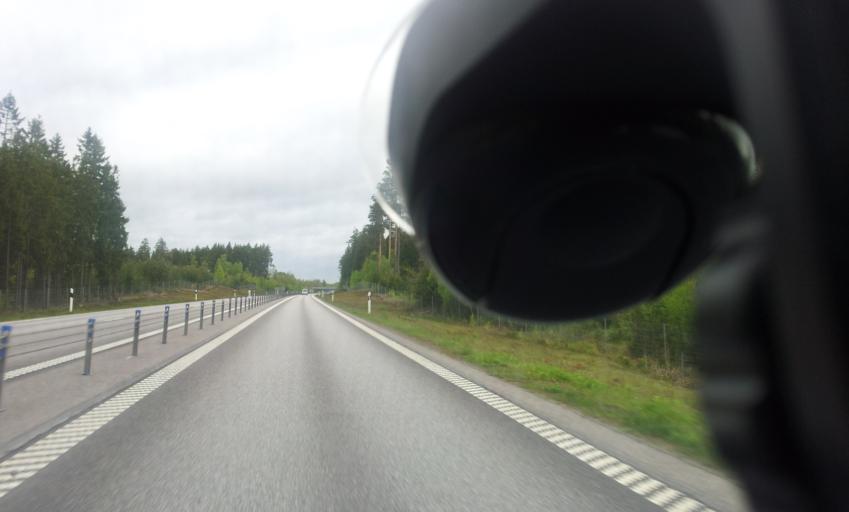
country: SE
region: Kalmar
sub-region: Kalmar Kommun
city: Ljungbyholm
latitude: 56.5421
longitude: 16.0839
